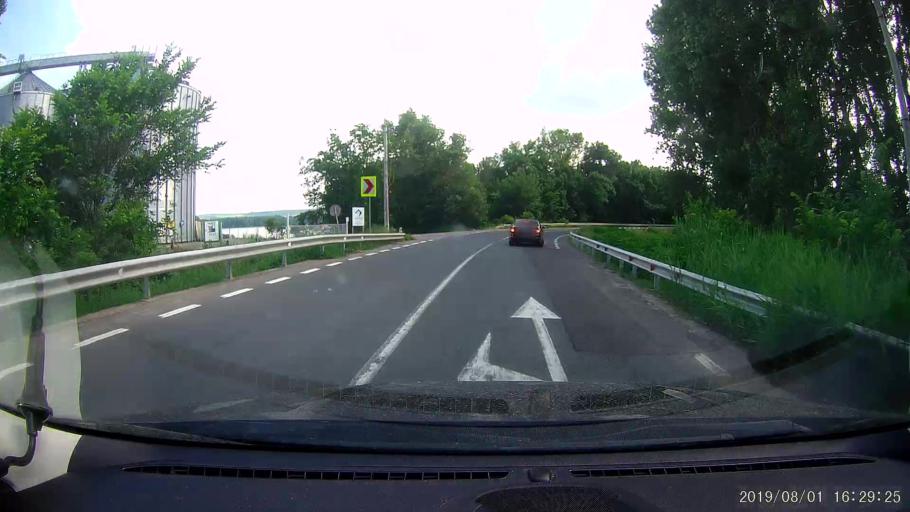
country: BG
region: Silistra
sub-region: Obshtina Silistra
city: Silistra
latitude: 44.1413
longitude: 27.2899
